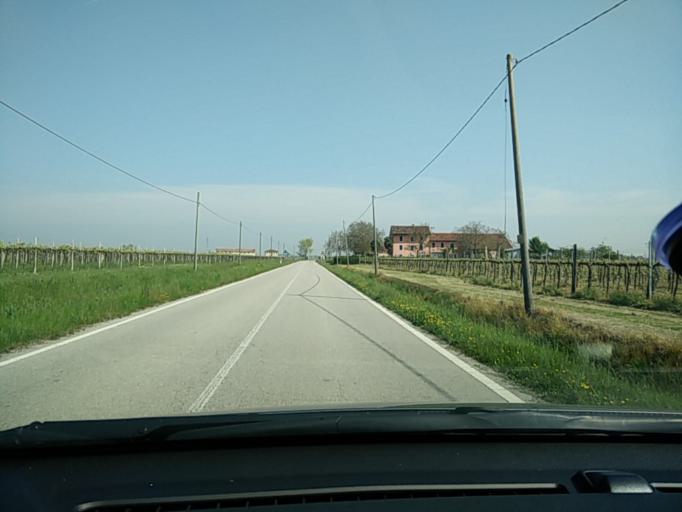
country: IT
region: Veneto
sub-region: Provincia di Treviso
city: Fornaci
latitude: 45.6659
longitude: 12.4428
